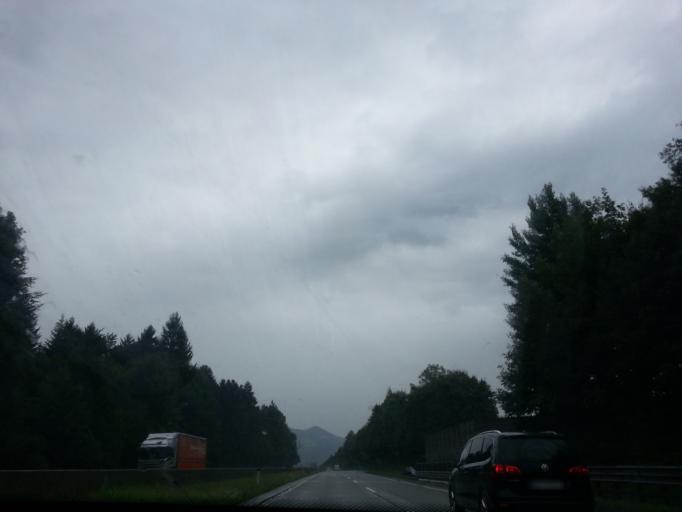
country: AT
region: Salzburg
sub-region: Politischer Bezirk Salzburg-Umgebung
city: Fuschl am See
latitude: 47.8442
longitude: 13.3004
